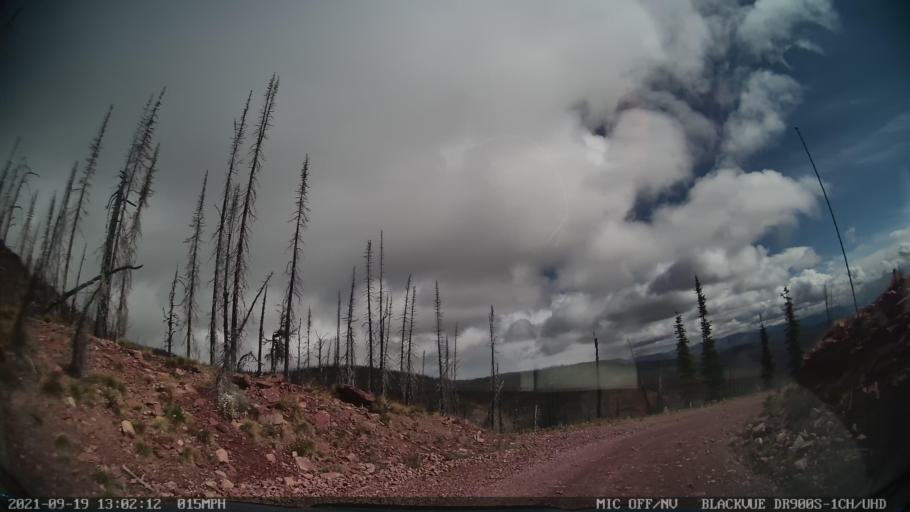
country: US
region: Montana
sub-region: Missoula County
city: Seeley Lake
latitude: 47.1891
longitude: -113.3537
